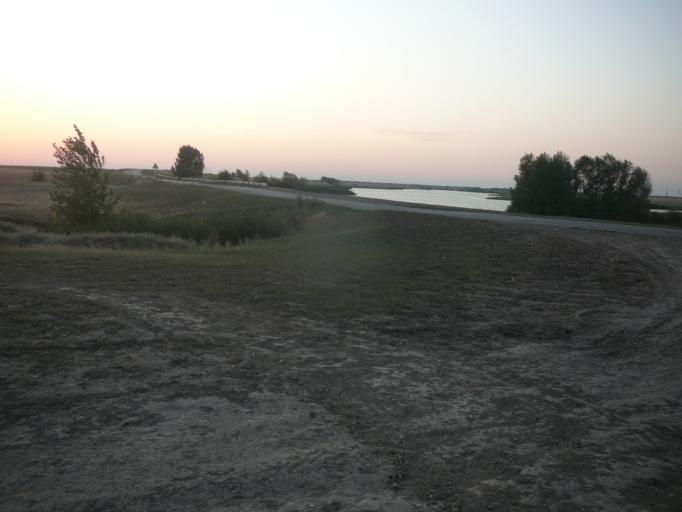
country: RU
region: Saratov
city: Stepnoye
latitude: 51.4263
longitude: 47.0037
